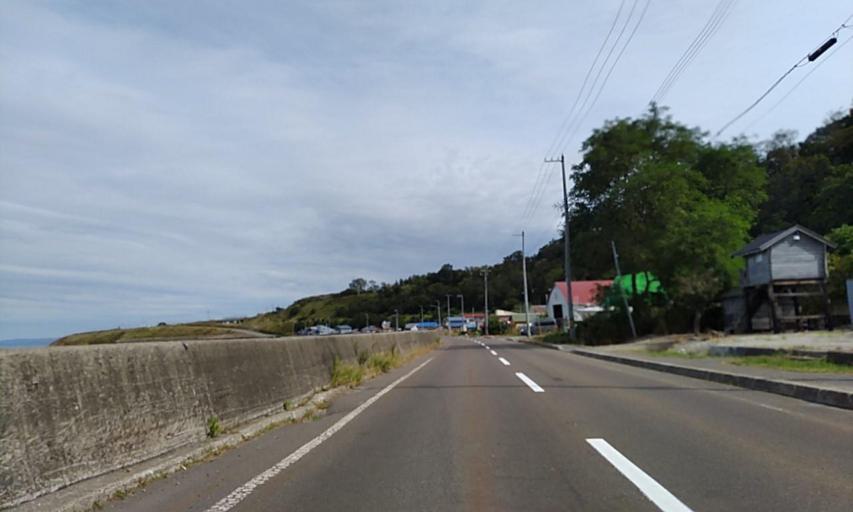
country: JP
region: Hokkaido
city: Rumoi
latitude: 43.8529
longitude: 141.5405
